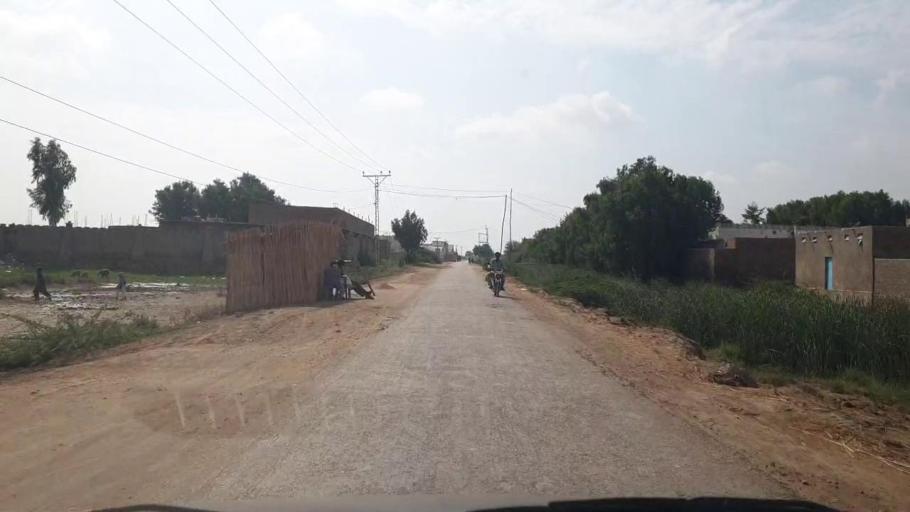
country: PK
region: Sindh
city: Kario
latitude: 24.6516
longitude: 68.5423
